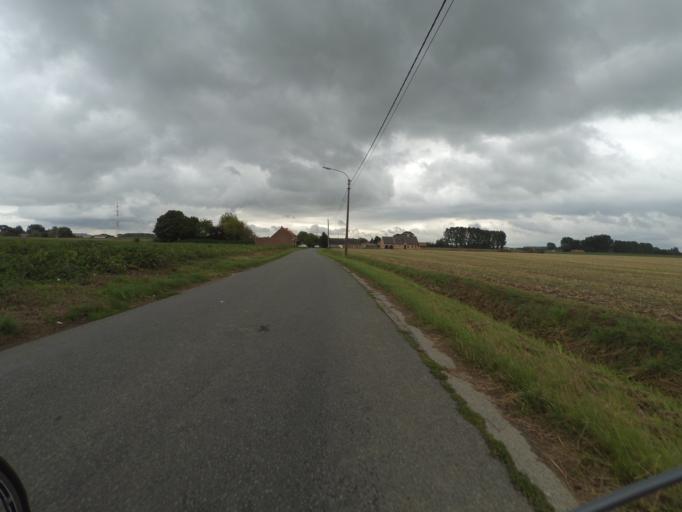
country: BE
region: Wallonia
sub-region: Province du Hainaut
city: Celles
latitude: 50.7398
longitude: 3.4645
